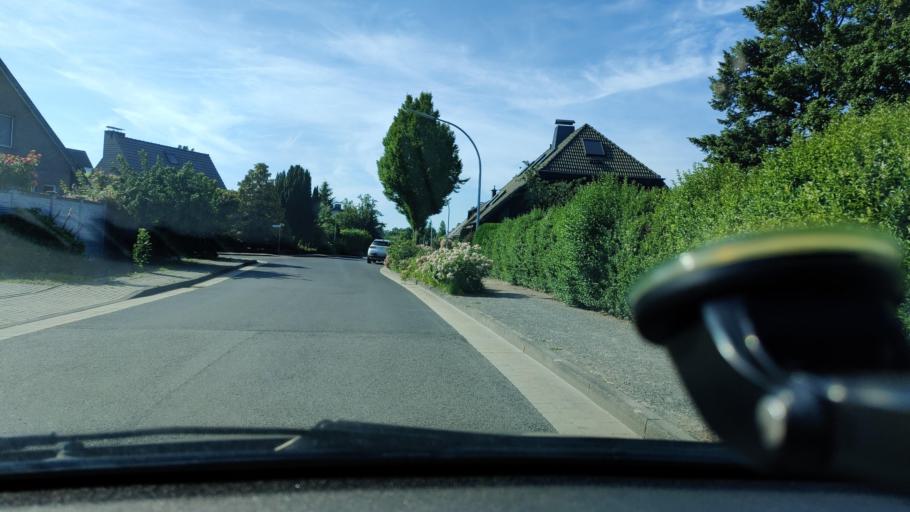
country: DE
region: North Rhine-Westphalia
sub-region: Regierungsbezirk Dusseldorf
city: Rheurdt
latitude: 51.5027
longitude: 6.4974
